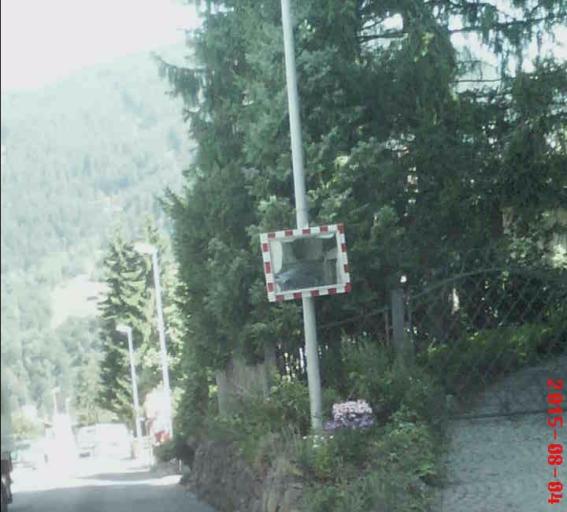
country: CH
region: Grisons
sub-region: Praettigau/Davos District
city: Klosters Serneus
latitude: 46.8720
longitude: 9.8799
